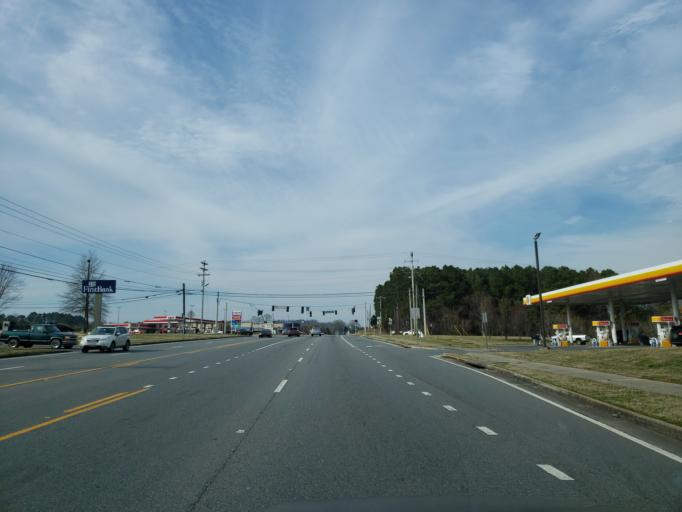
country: US
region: Georgia
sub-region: Whitfield County
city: Varnell
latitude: 34.8934
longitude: -84.9467
